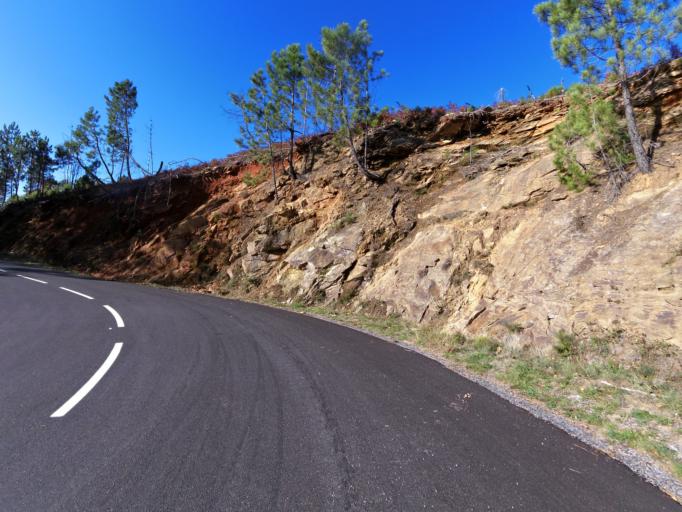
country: FR
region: Rhone-Alpes
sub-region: Departement de l'Ardeche
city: Lablachere
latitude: 44.4905
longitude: 4.1466
